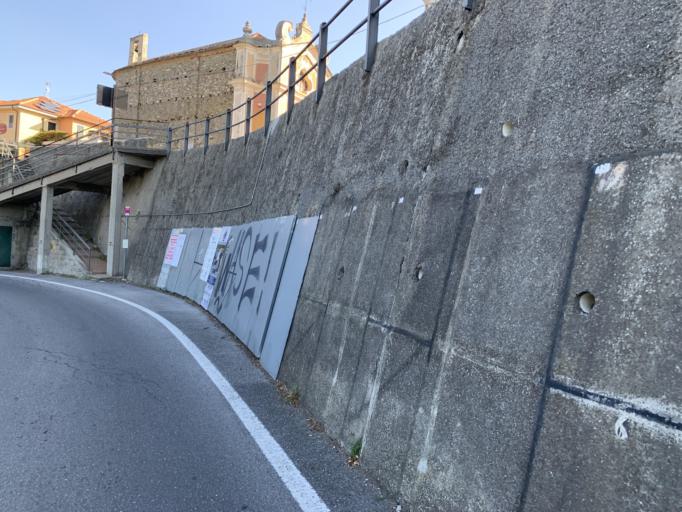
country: IT
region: Liguria
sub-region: Provincia di Savona
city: Tovo San Giacomo
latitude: 44.1864
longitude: 8.2708
